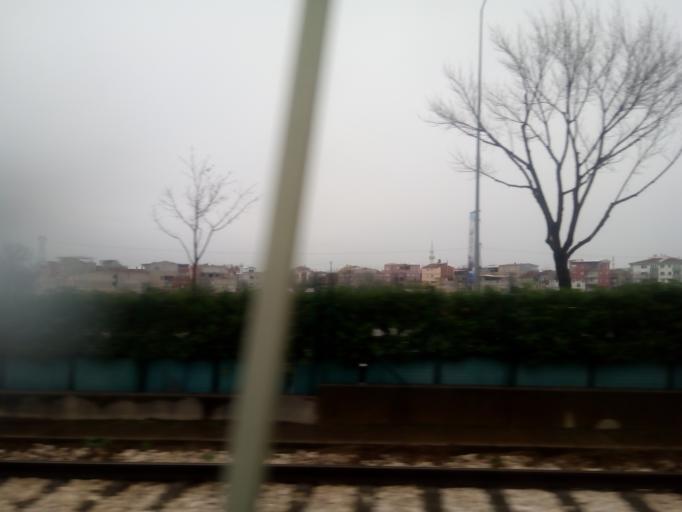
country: TR
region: Bursa
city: Yildirim
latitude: 40.2090
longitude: 29.0259
